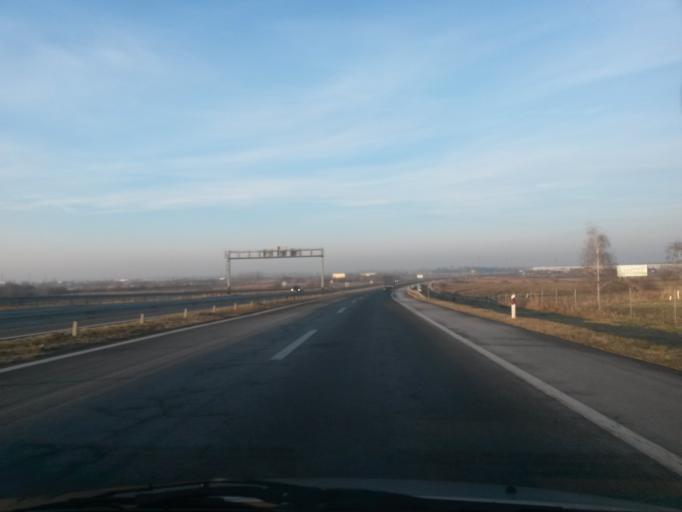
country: HR
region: Varazdinska
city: Jalzabet
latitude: 46.2512
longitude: 16.3999
